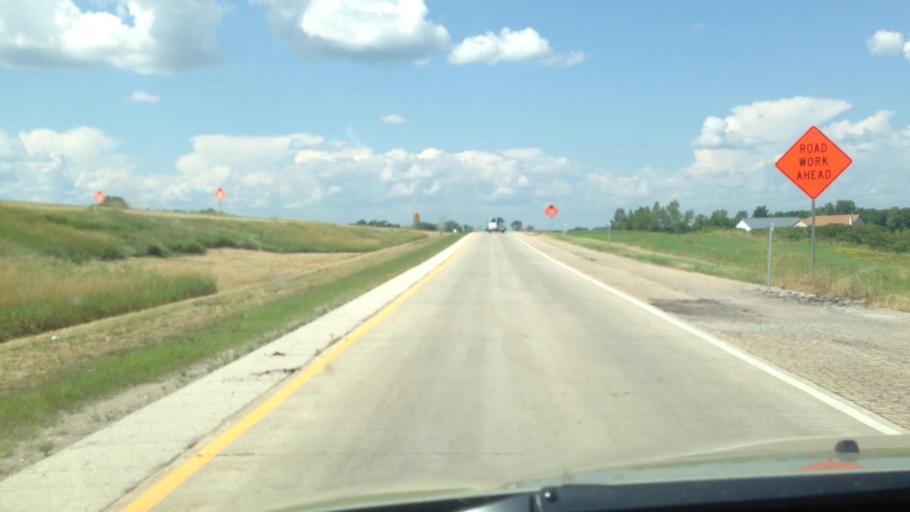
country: US
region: Wisconsin
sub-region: Brown County
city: Pulaski
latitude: 44.6743
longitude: -88.3081
